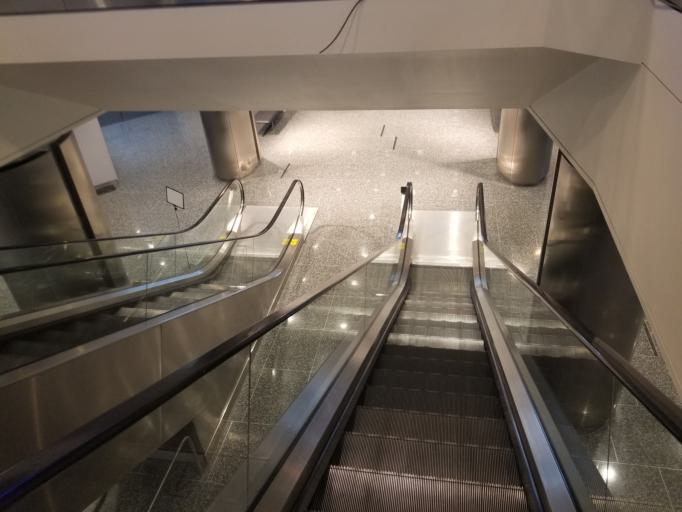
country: US
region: Michigan
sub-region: Wayne County
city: Detroit
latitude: 42.3294
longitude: -83.0402
